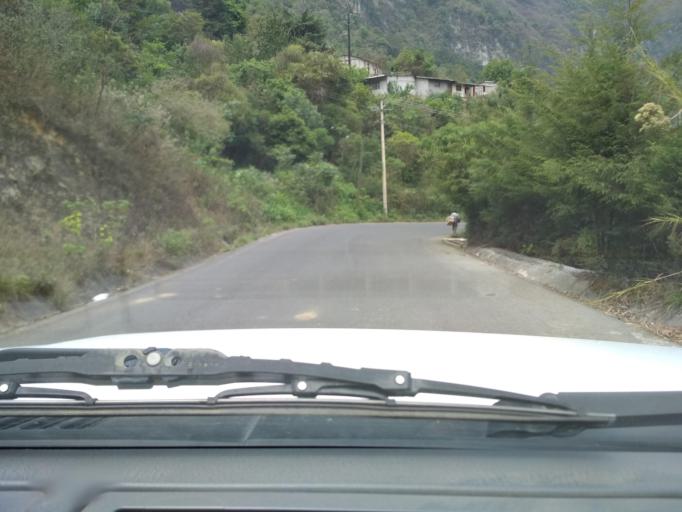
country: MX
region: Veracruz
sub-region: Camerino Z. Mendoza
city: La Cuesta
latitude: 18.7902
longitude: -97.1702
